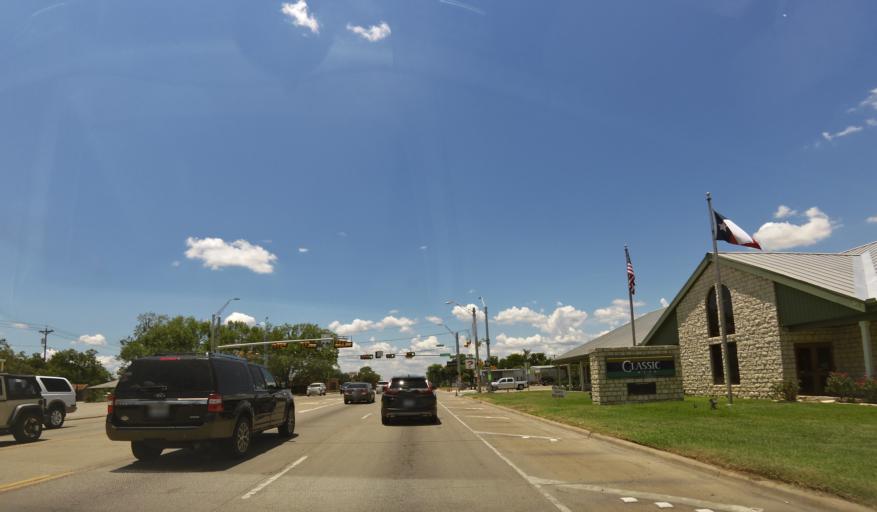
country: US
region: Texas
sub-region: Lee County
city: Giddings
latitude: 30.1816
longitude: -96.9295
